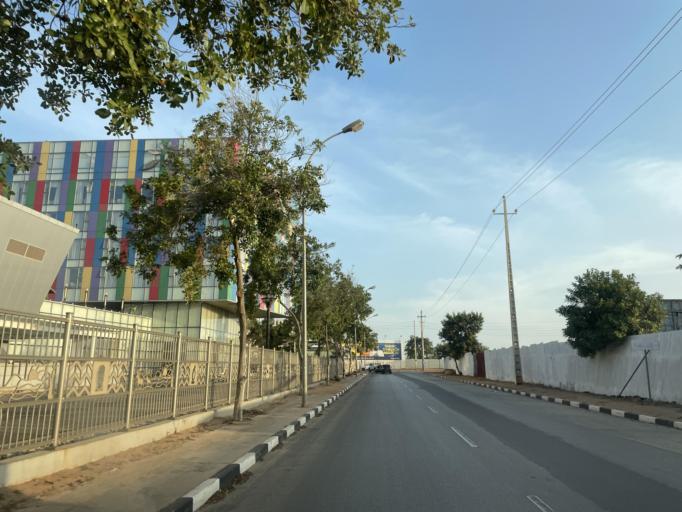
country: AO
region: Luanda
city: Luanda
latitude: -8.9160
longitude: 13.1957
